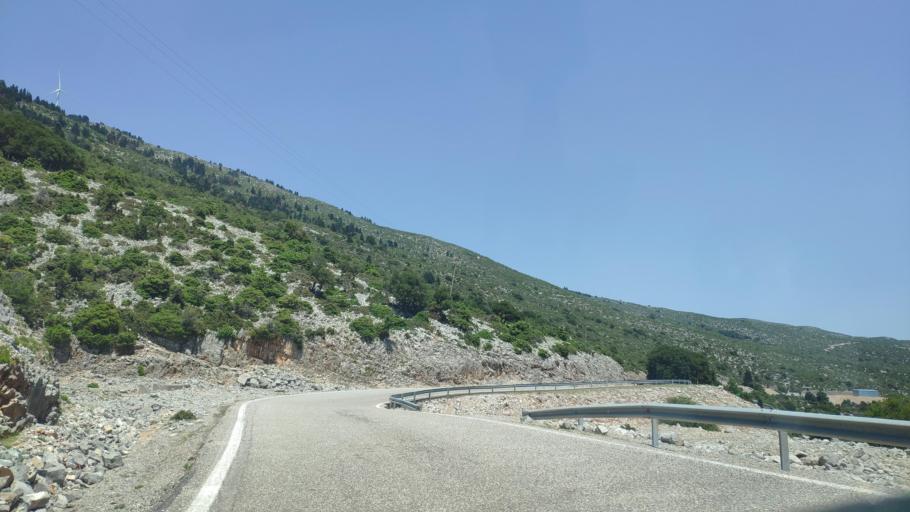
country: GR
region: West Greece
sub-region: Nomos Aitolias kai Akarnanias
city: Krikellos
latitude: 39.0625
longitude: 21.3825
